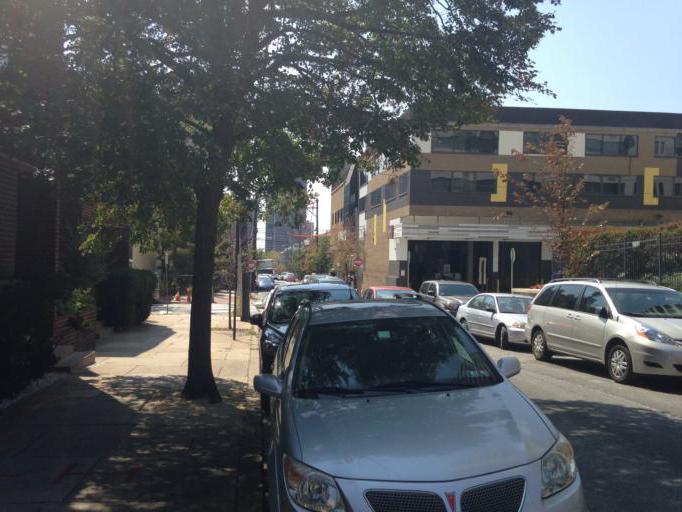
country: US
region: Pennsylvania
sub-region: Philadelphia County
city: Philadelphia
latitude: 39.9625
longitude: -75.1714
